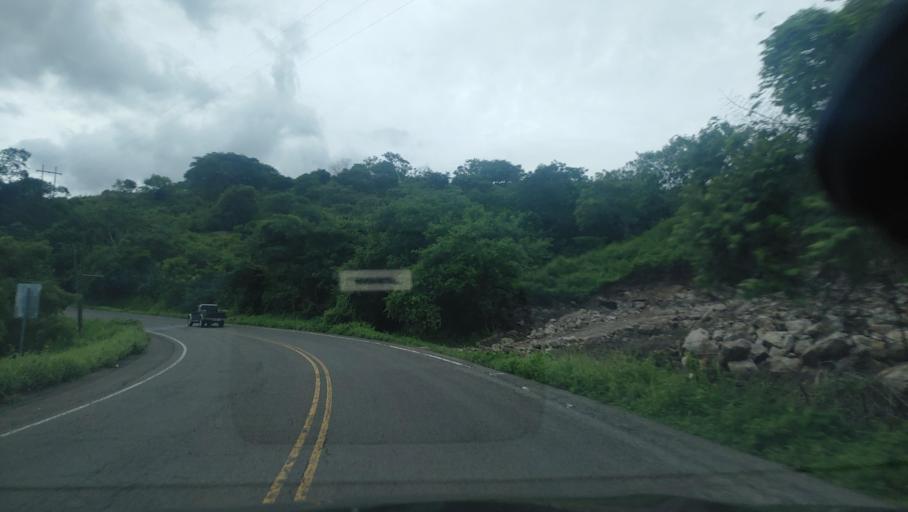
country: HN
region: Choluteca
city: Santa Ana de Yusguare
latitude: 13.3723
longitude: -87.0695
